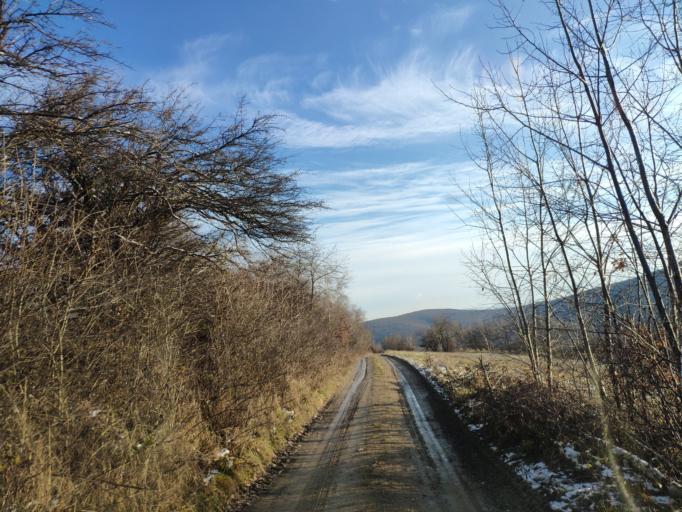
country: SK
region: Kosicky
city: Moldava nad Bodvou
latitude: 48.7372
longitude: 21.0904
